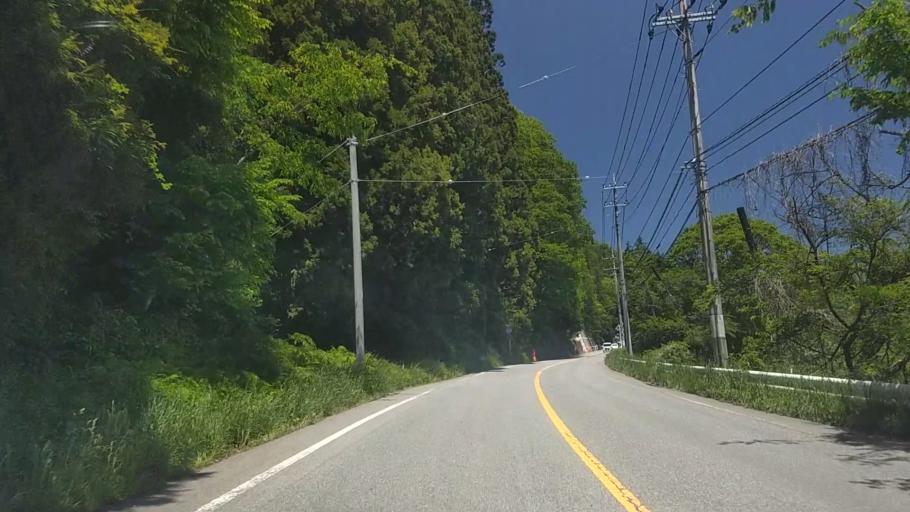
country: JP
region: Yamanashi
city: Nirasaki
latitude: 35.8794
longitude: 138.4272
